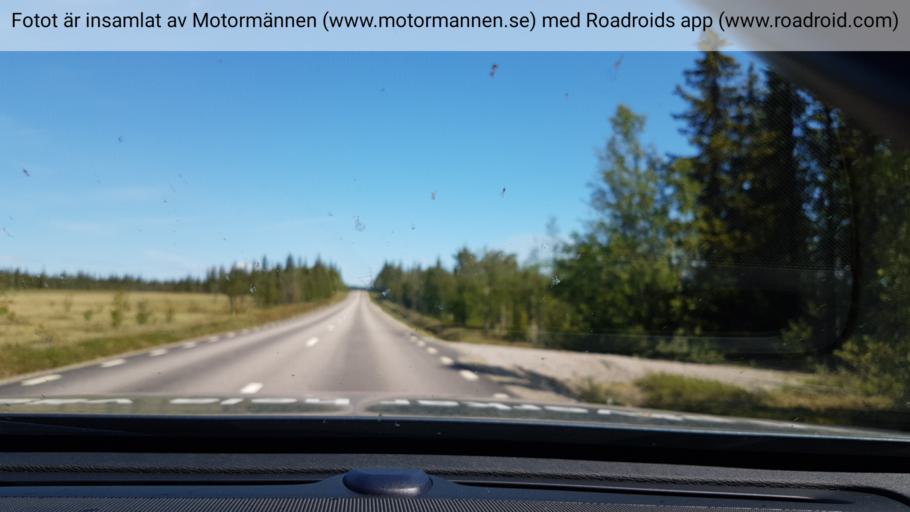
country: SE
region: Vaesterbotten
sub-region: Asele Kommun
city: Insjon
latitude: 64.7300
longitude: 17.4723
